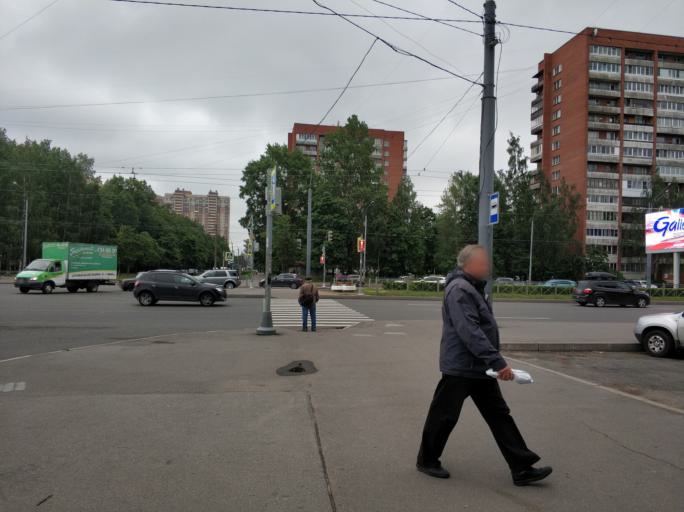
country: RU
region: St.-Petersburg
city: Grazhdanka
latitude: 60.0341
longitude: 30.3934
